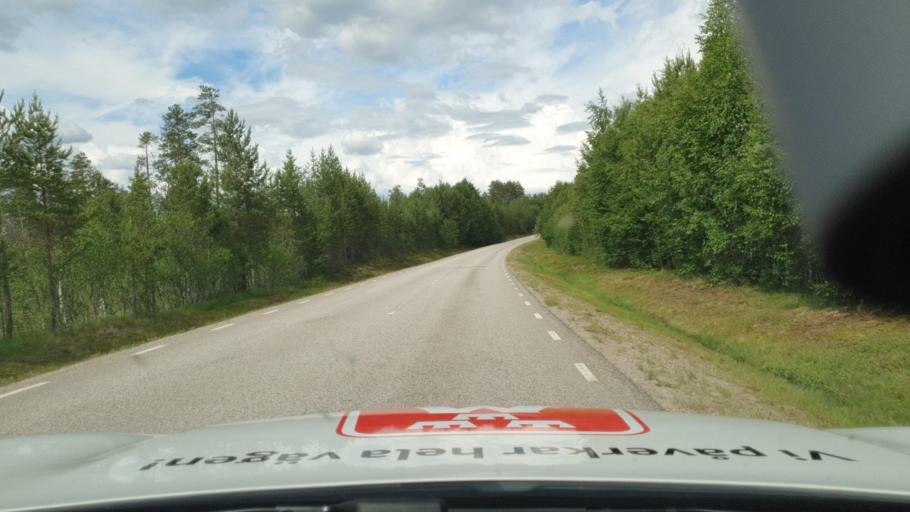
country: NO
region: Hedmark
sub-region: Trysil
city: Innbygda
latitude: 60.9577
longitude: 12.4693
